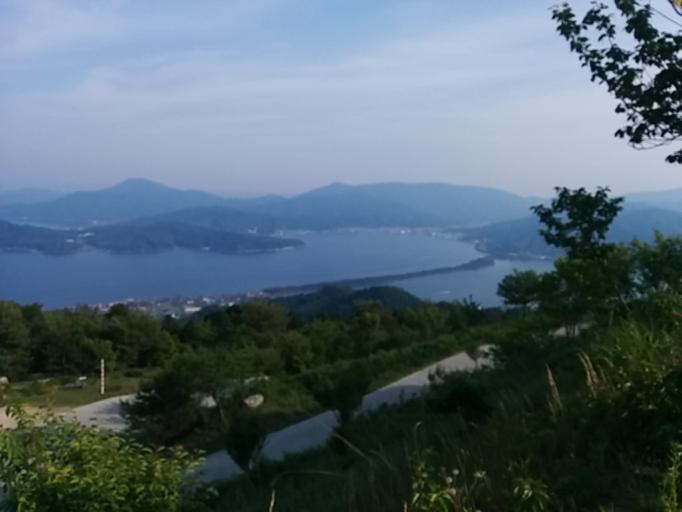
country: JP
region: Kyoto
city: Miyazu
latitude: 35.5765
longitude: 135.2061
